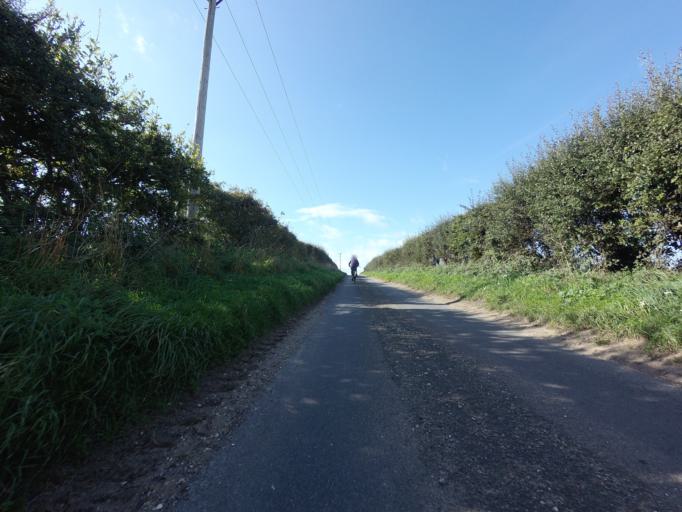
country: GB
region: England
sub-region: Norfolk
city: Hunstanton
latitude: 52.9360
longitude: 0.6035
